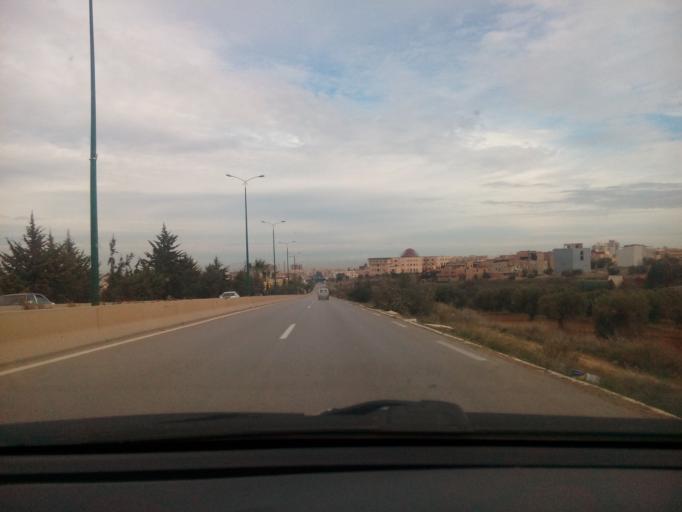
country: DZ
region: Tlemcen
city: Mansoura
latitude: 34.8733
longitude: -1.3494
